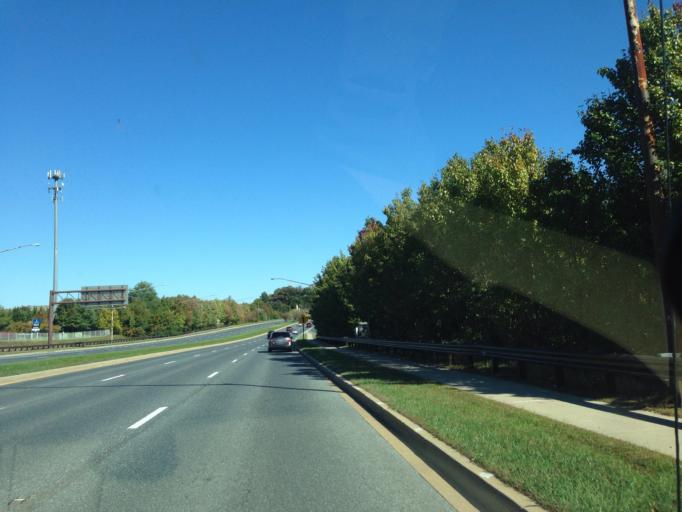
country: US
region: Maryland
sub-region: Montgomery County
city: Germantown
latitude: 39.1989
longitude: -77.2607
